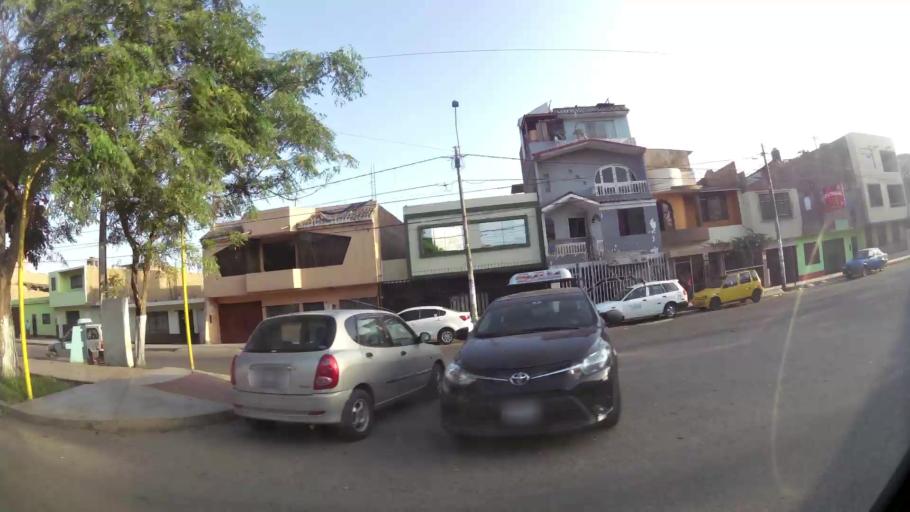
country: PE
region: La Libertad
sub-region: Provincia de Trujillo
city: El Porvenir
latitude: -8.0881
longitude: -78.9975
